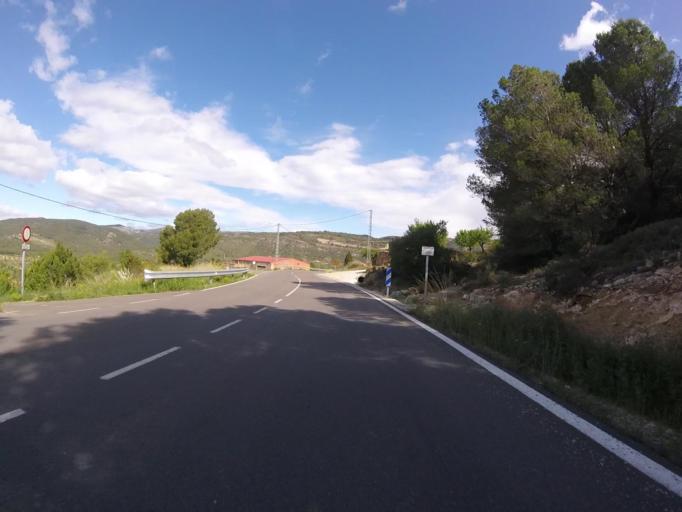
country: ES
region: Valencia
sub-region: Provincia de Castello
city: Culla
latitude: 40.2787
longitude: -0.1118
